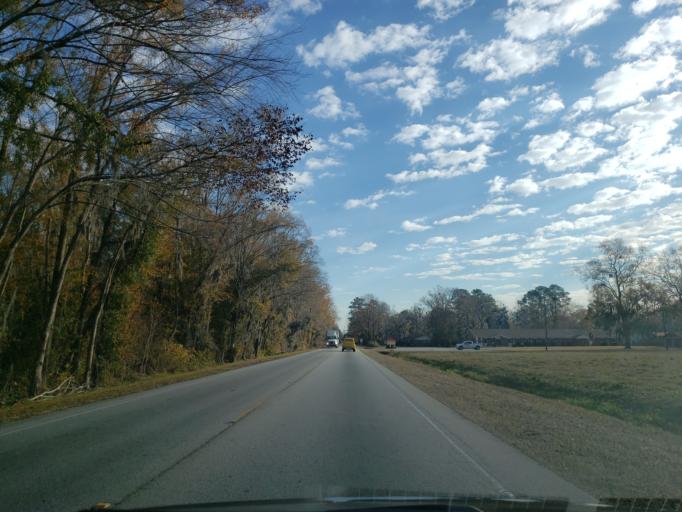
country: US
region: Georgia
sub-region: Chatham County
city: Port Wentworth
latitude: 32.1550
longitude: -81.1744
